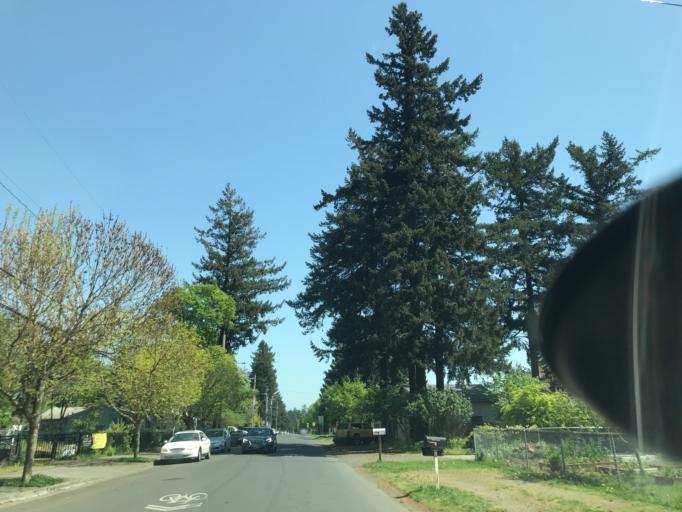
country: US
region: Oregon
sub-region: Multnomah County
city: Lents
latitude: 45.4949
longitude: -122.5556
